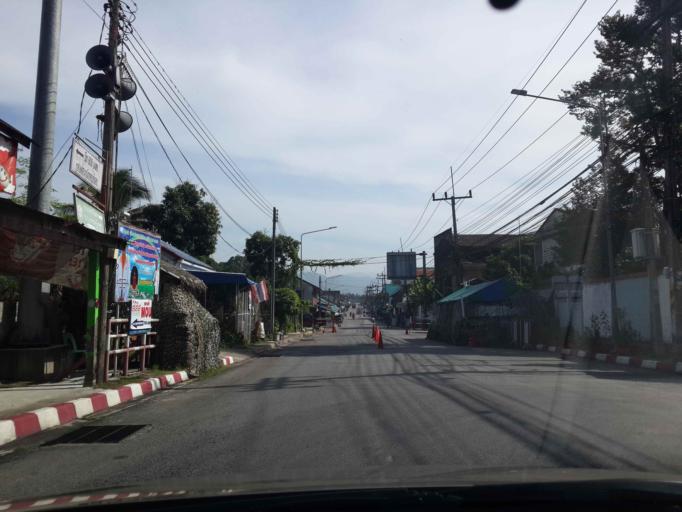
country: TH
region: Narathiwat
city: Rueso
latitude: 6.3855
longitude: 101.5129
